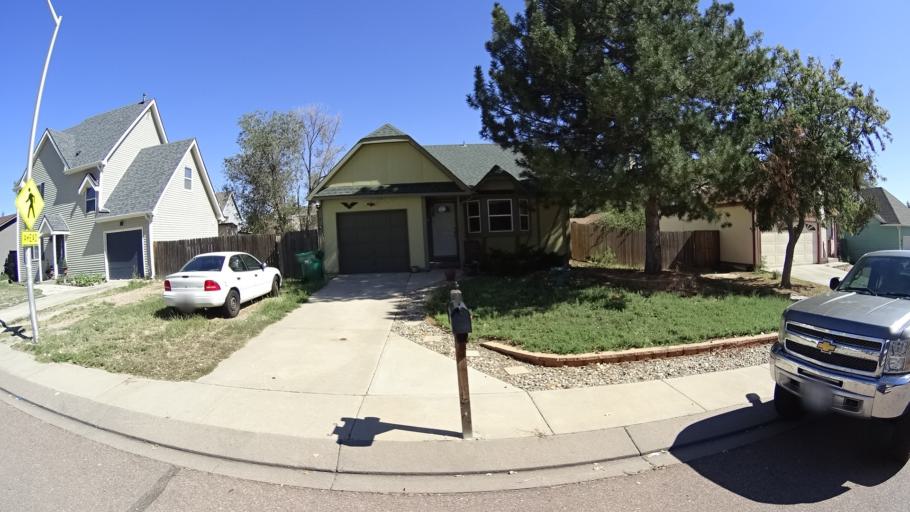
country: US
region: Colorado
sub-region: El Paso County
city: Stratmoor
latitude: 38.7833
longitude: -104.7468
